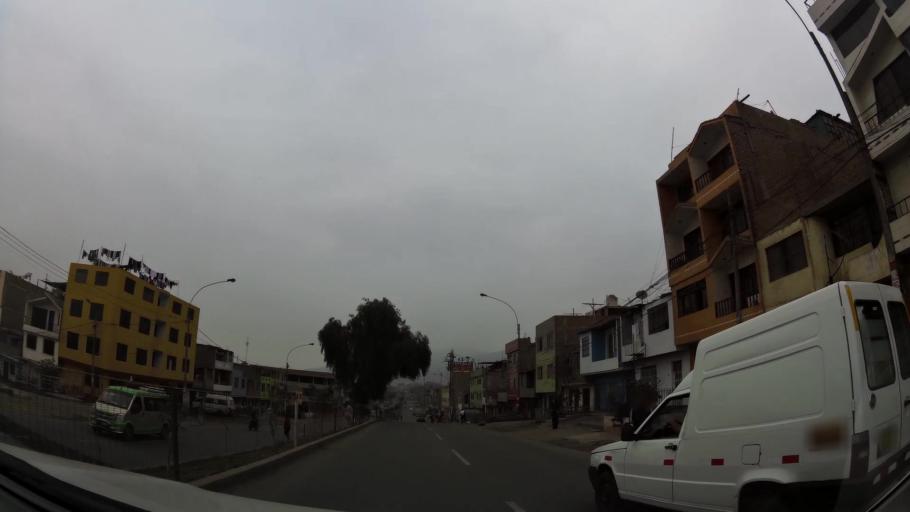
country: PE
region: Lima
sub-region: Lima
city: Independencia
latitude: -11.9616
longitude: -77.0070
